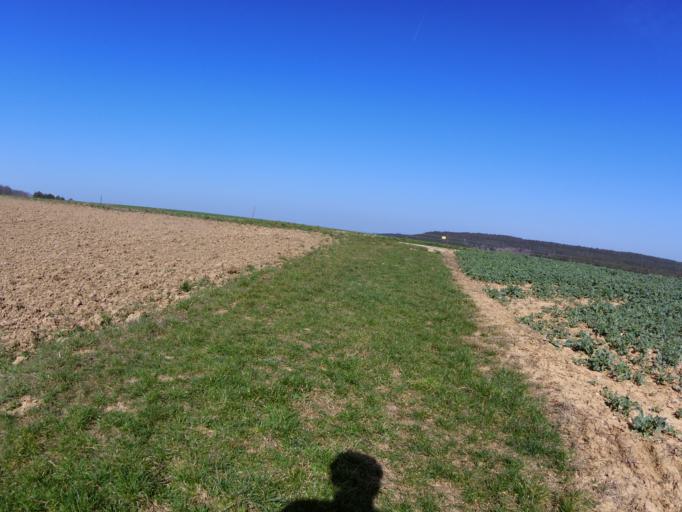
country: DE
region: Bavaria
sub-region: Regierungsbezirk Unterfranken
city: Erlabrunn
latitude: 49.8502
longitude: 9.8316
